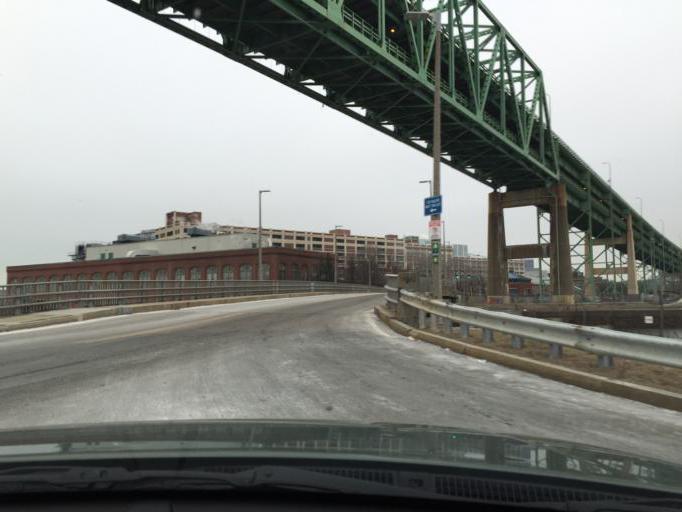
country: US
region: Massachusetts
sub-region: Suffolk County
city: Chelsea
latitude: 42.3810
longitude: -71.0518
